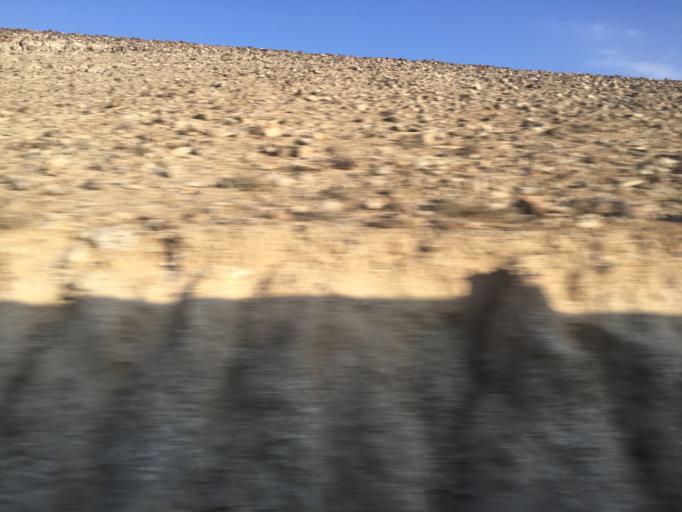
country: IL
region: Southern District
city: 'Arad
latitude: 31.3046
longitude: 35.2535
